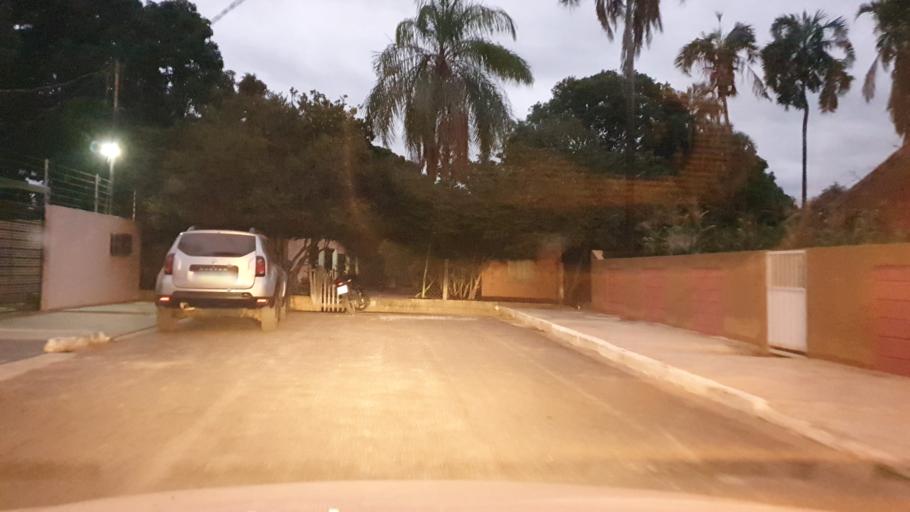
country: BR
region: Mato Grosso
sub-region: Pontes E Lacerda
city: Pontes e Lacerda
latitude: -15.2325
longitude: -59.3155
